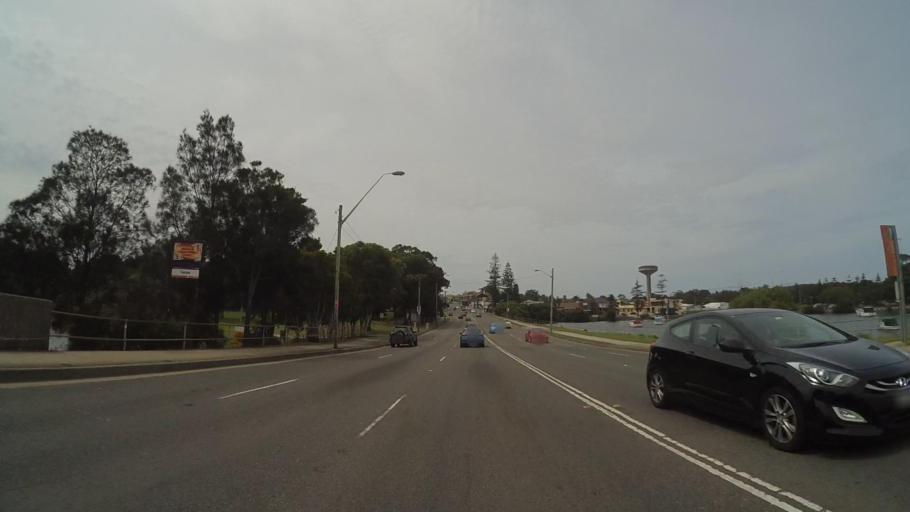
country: AU
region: New South Wales
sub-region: Rockdale
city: Arncliffe
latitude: -33.9285
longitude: 151.1572
